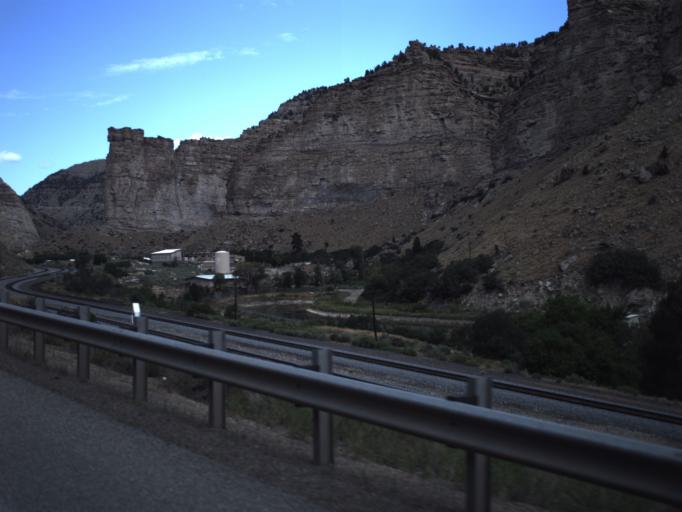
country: US
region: Utah
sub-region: Carbon County
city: Helper
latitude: 39.7419
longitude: -110.8778
